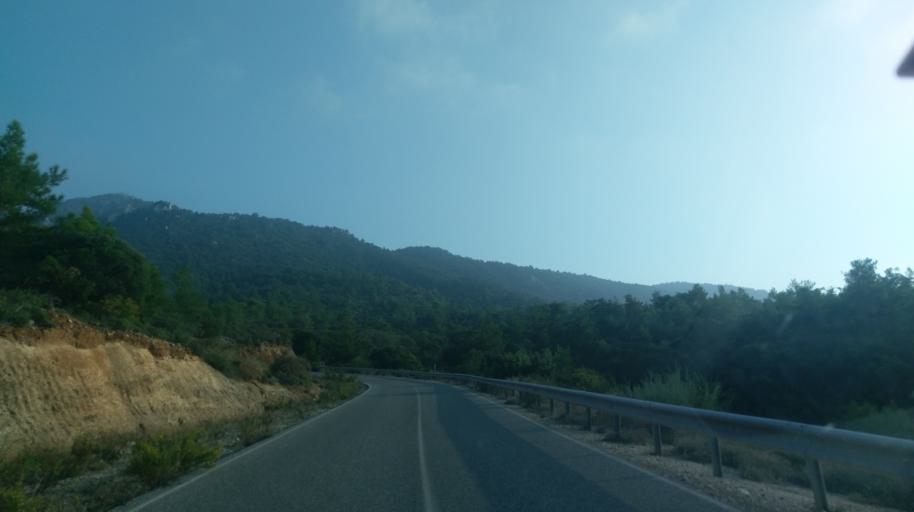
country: CY
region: Ammochostos
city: Trikomo
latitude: 35.4109
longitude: 33.9042
